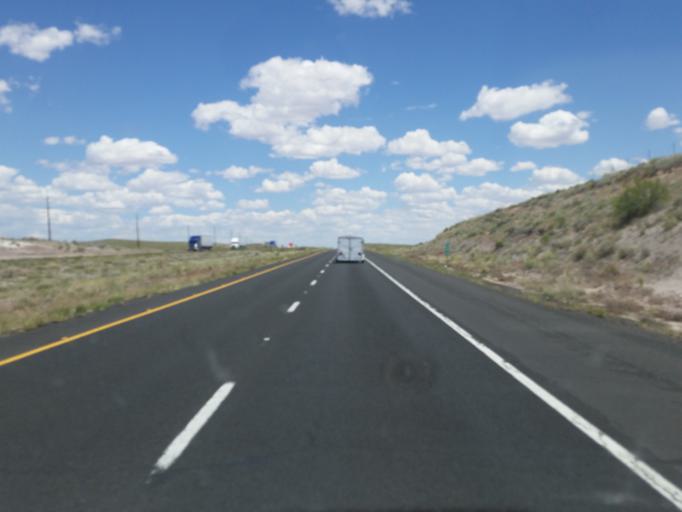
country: US
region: Arizona
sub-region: Navajo County
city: Holbrook
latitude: 34.9908
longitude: -109.9814
